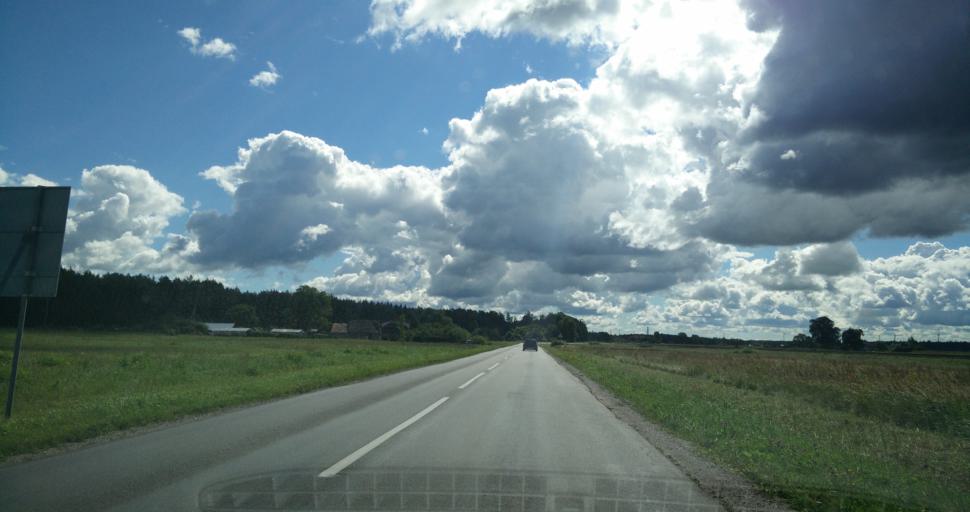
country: LT
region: Klaipedos apskritis
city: Silute
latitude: 55.3301
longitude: 21.5182
